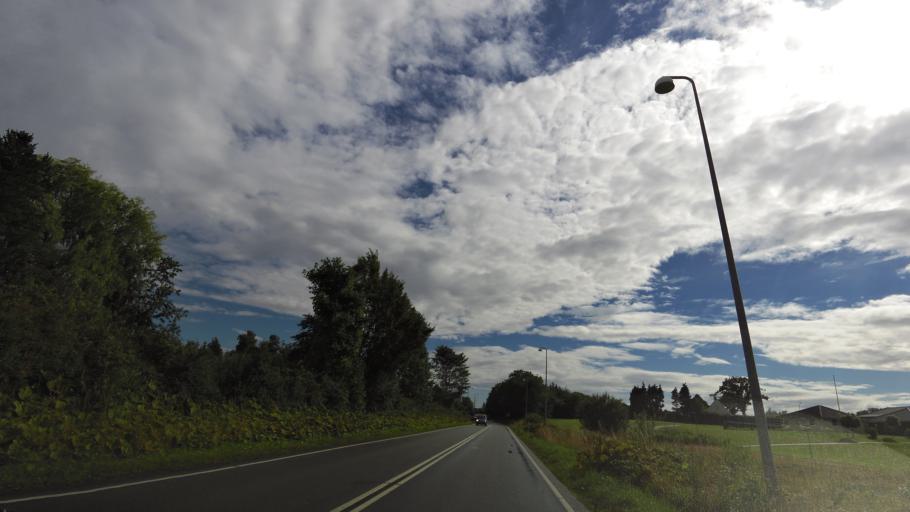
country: DK
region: South Denmark
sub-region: Assens Kommune
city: Vissenbjerg
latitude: 55.4477
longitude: 10.1848
